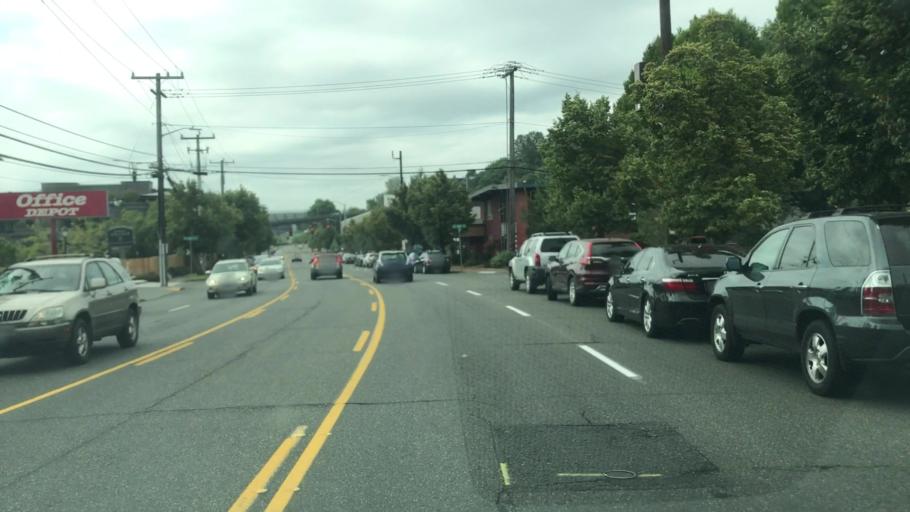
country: US
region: Washington
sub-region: King County
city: Seattle
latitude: 47.6649
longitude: -122.3009
